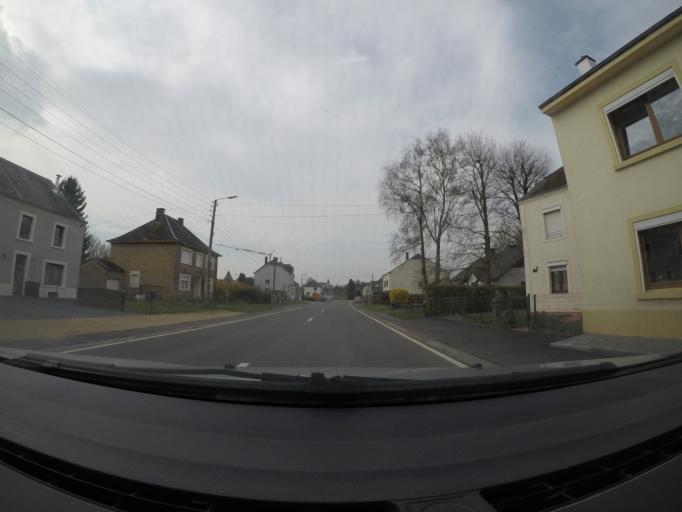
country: BE
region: Wallonia
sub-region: Province du Luxembourg
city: Chiny
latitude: 49.7034
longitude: 5.4233
